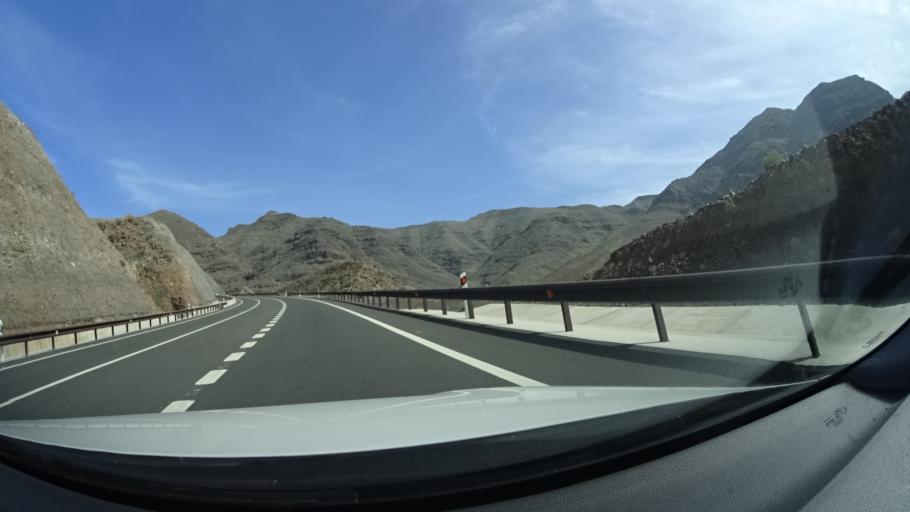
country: ES
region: Canary Islands
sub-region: Provincia de Las Palmas
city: San Nicolas
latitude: 28.0147
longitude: -15.7719
